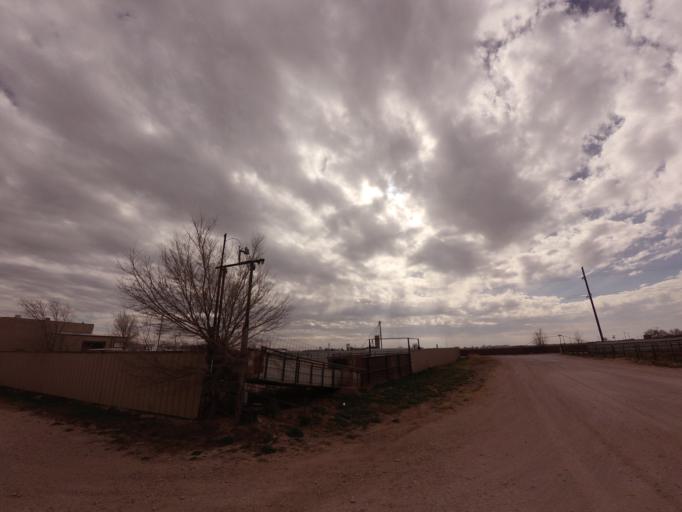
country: US
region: New Mexico
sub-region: Curry County
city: Clovis
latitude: 34.3908
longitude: -103.2218
